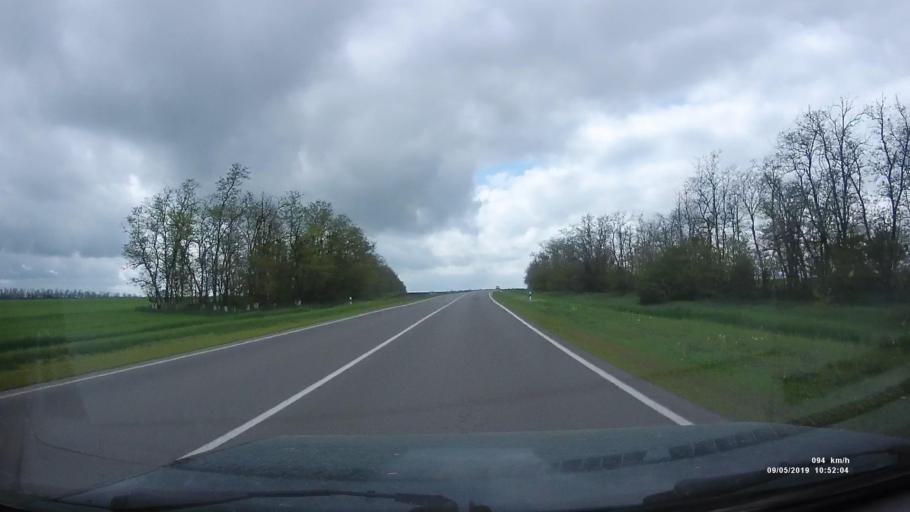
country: RU
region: Rostov
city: Peshkovo
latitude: 46.9058
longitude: 39.3548
